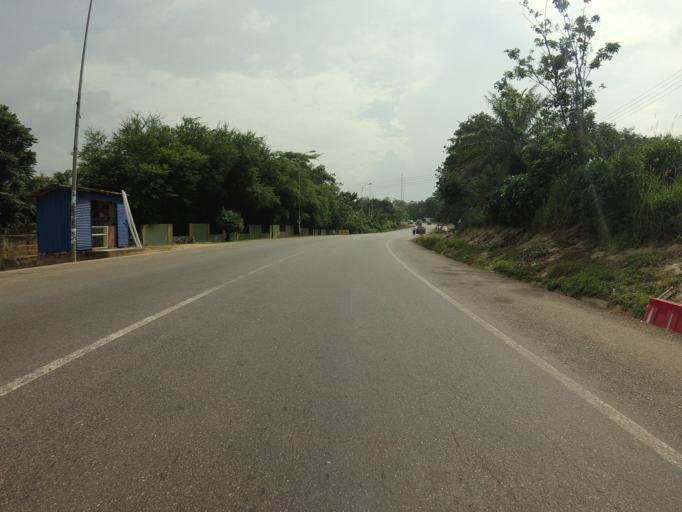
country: GH
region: Eastern
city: Aburi
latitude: 5.8164
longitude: -0.1870
